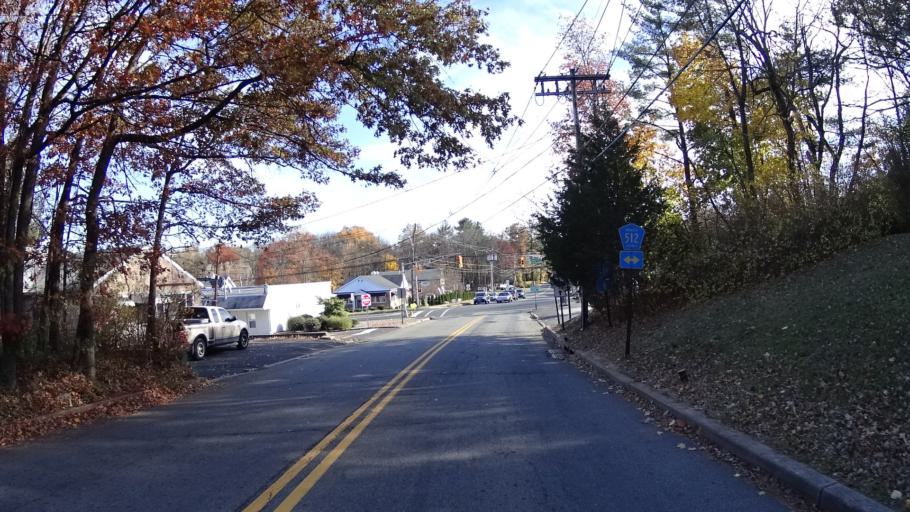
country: US
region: New Jersey
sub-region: Union County
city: Berkeley Heights
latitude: 40.6747
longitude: -74.4665
